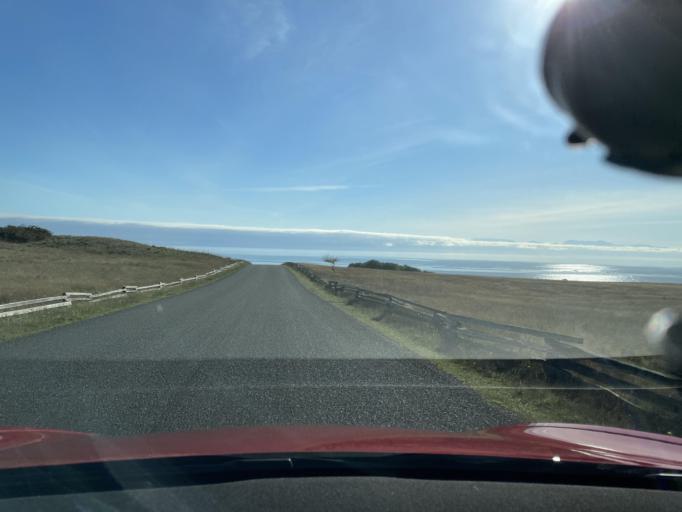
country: US
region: Washington
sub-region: San Juan County
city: Friday Harbor
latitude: 48.4602
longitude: -123.0016
